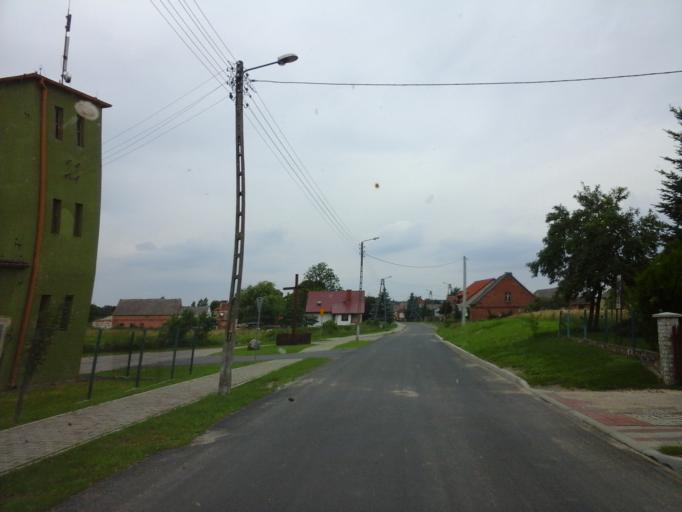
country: PL
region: West Pomeranian Voivodeship
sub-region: Powiat choszczenski
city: Krzecin
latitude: 53.0798
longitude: 15.5571
